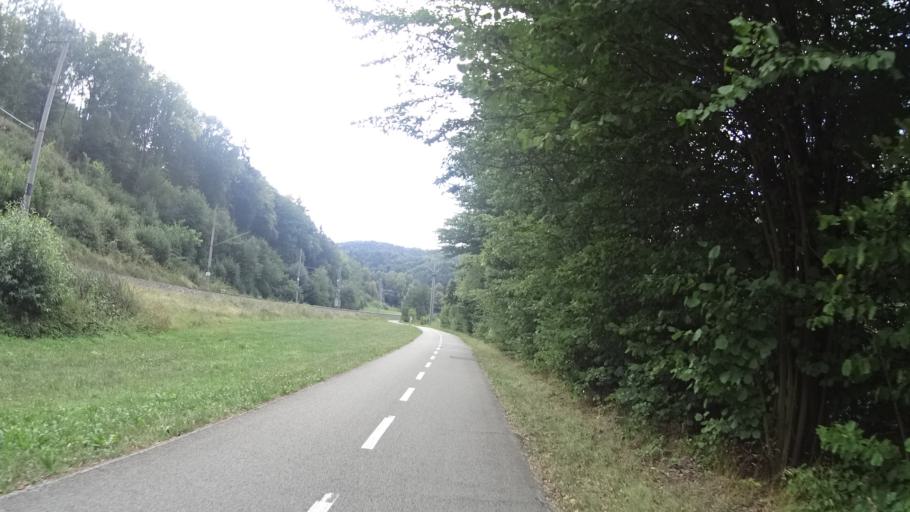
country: CZ
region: Pardubicky
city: Dolni Dobrouc
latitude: 49.9965
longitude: 16.4508
